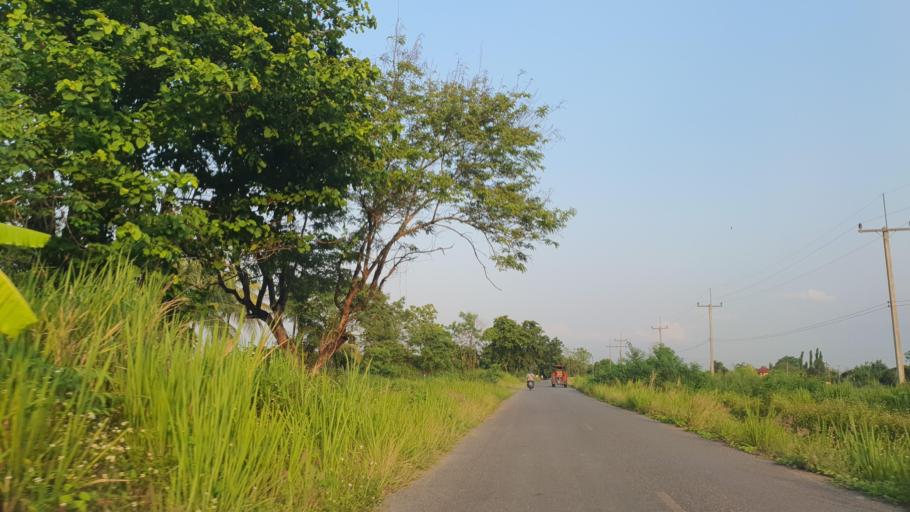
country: TH
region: Chiang Mai
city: Hang Dong
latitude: 18.6580
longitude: 98.9281
